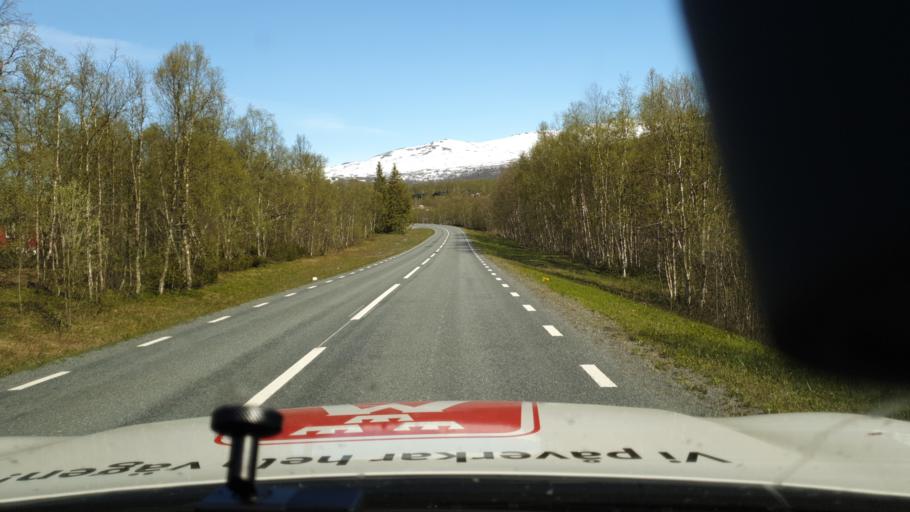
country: NO
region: Nordland
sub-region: Rana
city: Mo i Rana
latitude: 65.7780
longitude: 15.1123
